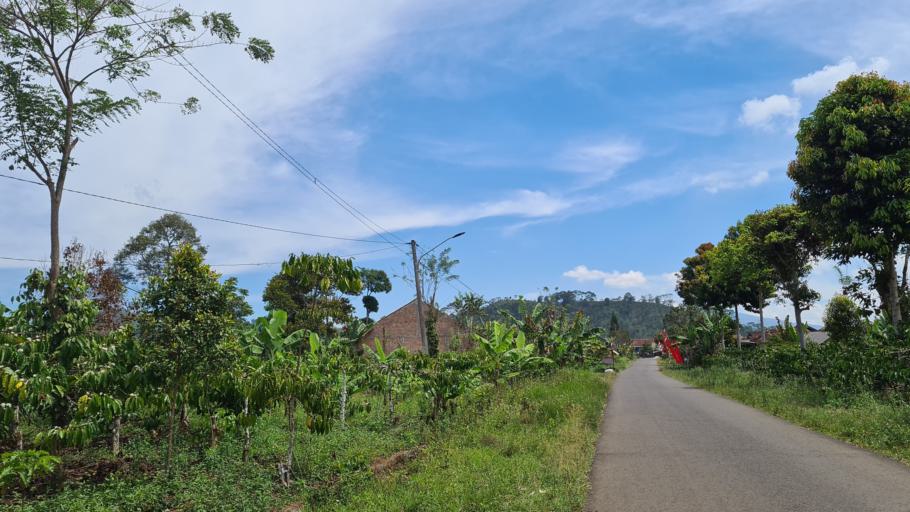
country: ID
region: Lampung
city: Kenali
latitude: -5.0958
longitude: 104.4259
